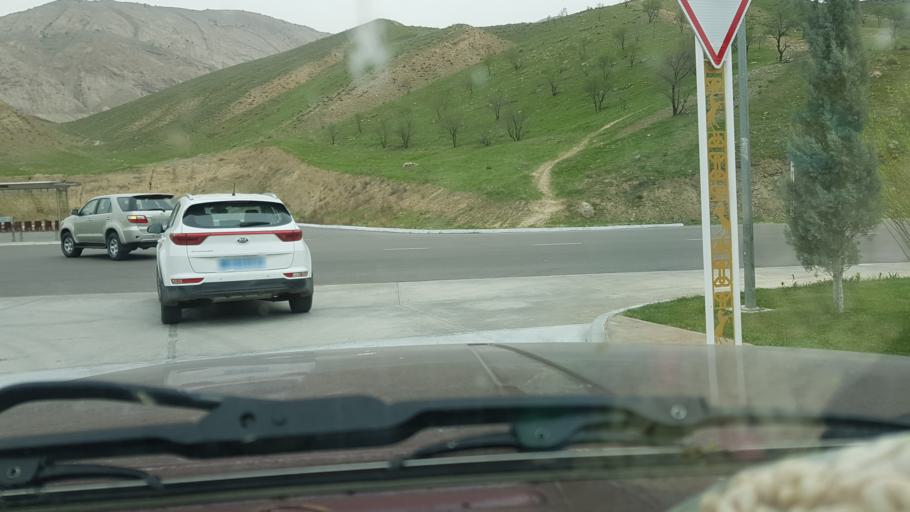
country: TM
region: Ahal
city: Arcabil
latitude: 38.0037
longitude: 58.0080
